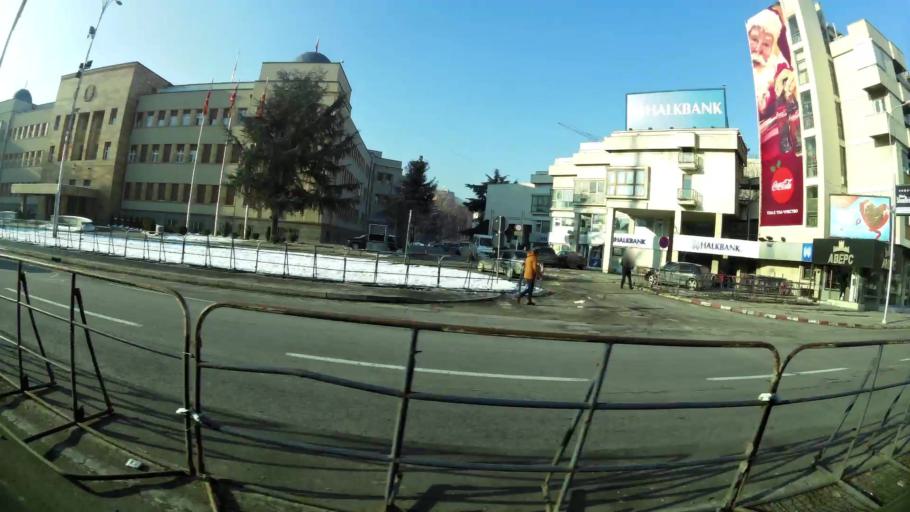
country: MK
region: Karpos
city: Skopje
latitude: 41.9942
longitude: 21.4336
